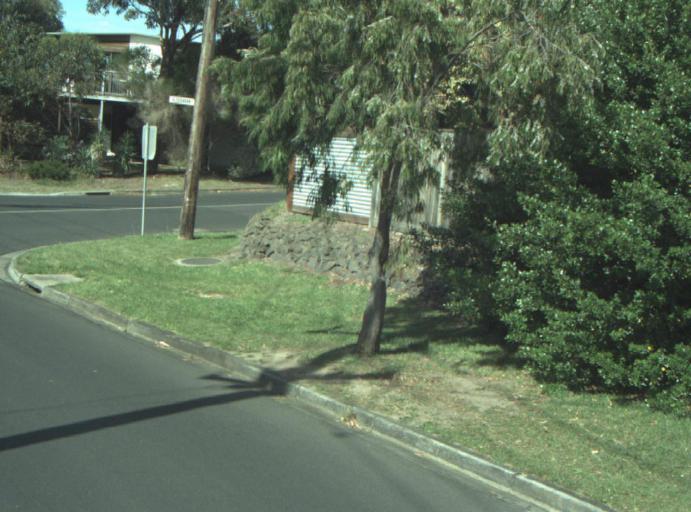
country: AU
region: Victoria
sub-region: Greater Geelong
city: Leopold
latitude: -38.2658
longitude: 144.5440
